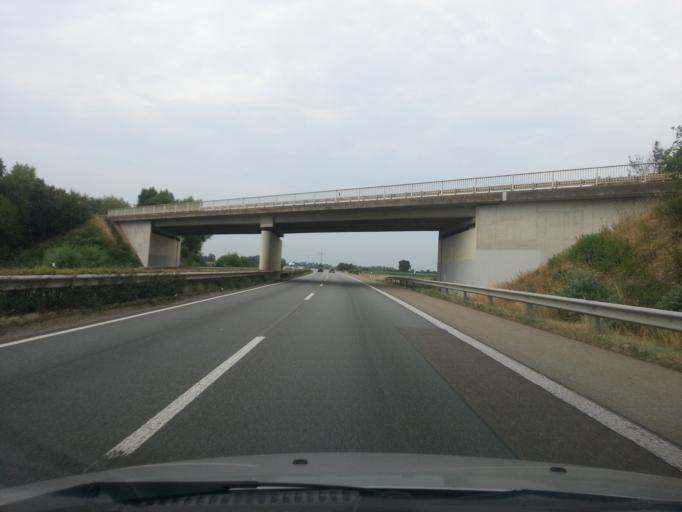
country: DE
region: Rheinland-Pfalz
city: Hochdorf-Assenheim
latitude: 49.4088
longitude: 8.2818
